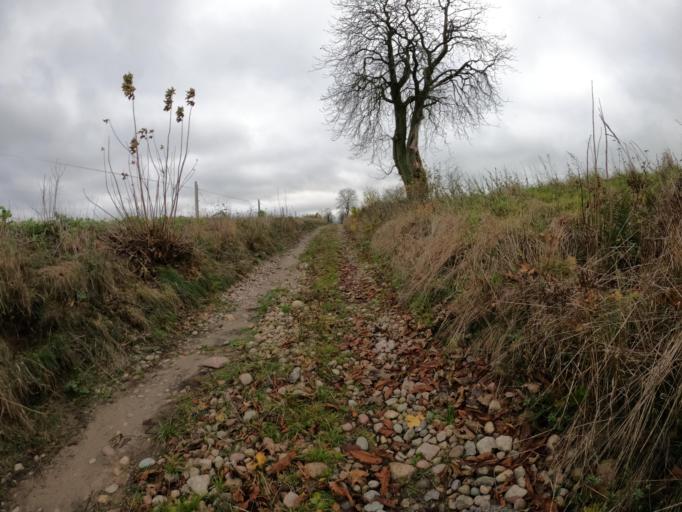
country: PL
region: West Pomeranian Voivodeship
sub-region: Powiat walecki
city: Tuczno
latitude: 53.2499
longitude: 16.2037
